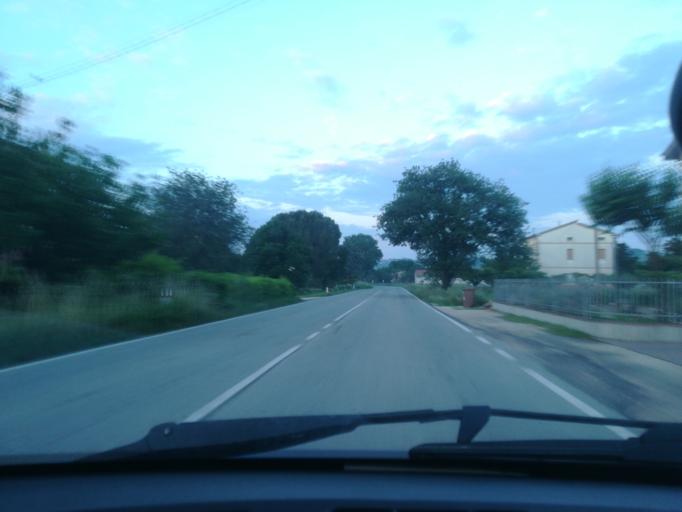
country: IT
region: The Marches
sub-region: Provincia di Macerata
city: Pollenza
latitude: 43.2920
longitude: 13.3654
